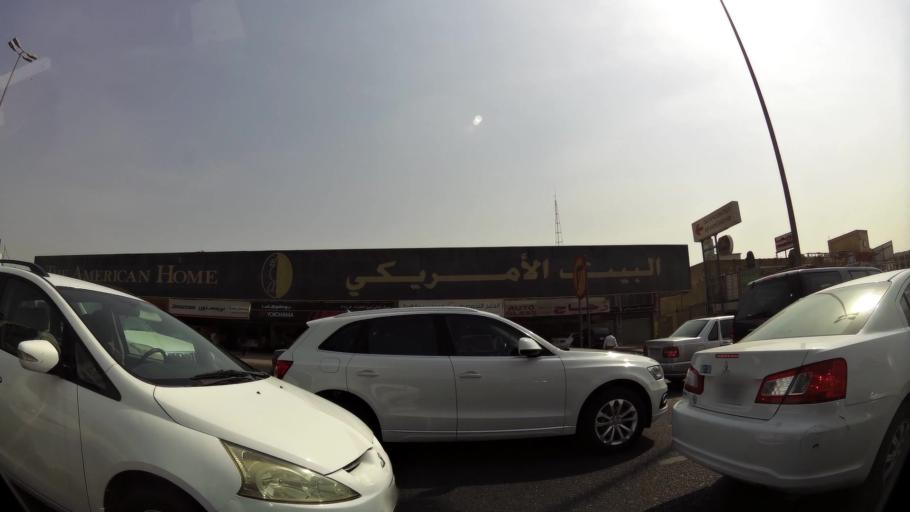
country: KW
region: Al Asimah
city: Ar Rabiyah
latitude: 29.3254
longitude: 47.9388
